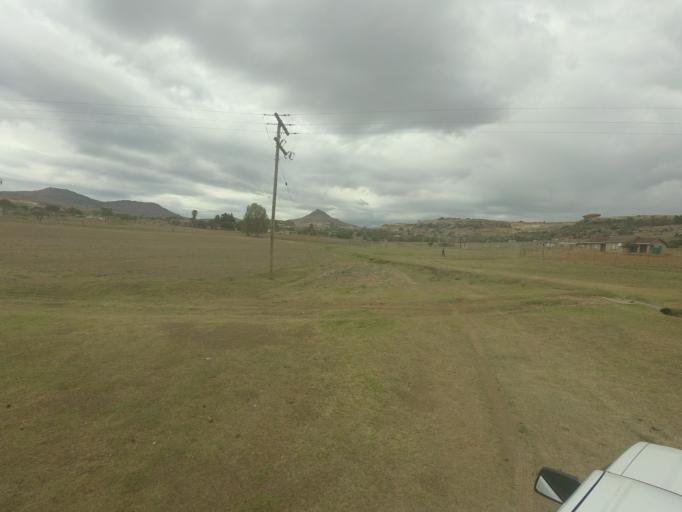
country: LS
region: Leribe
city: Leribe
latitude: -29.0258
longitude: 28.0215
